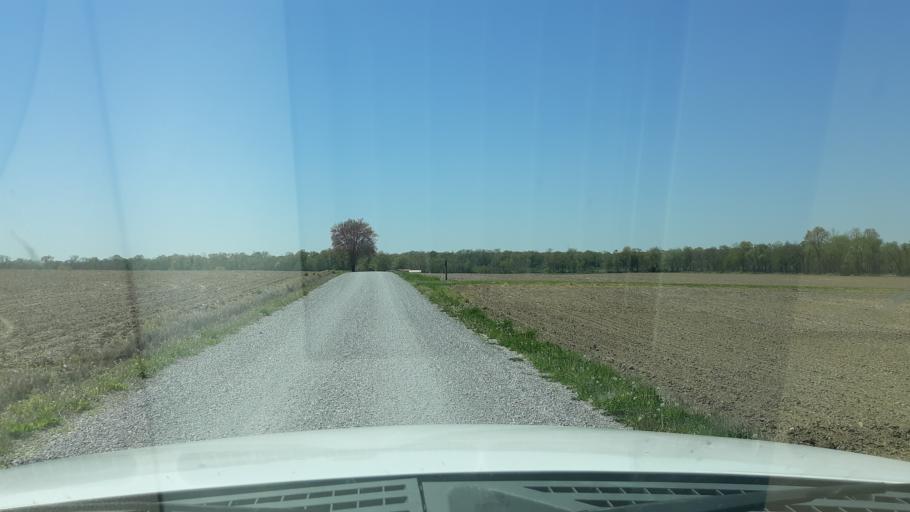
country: US
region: Illinois
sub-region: Saline County
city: Harrisburg
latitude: 37.8922
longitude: -88.6716
